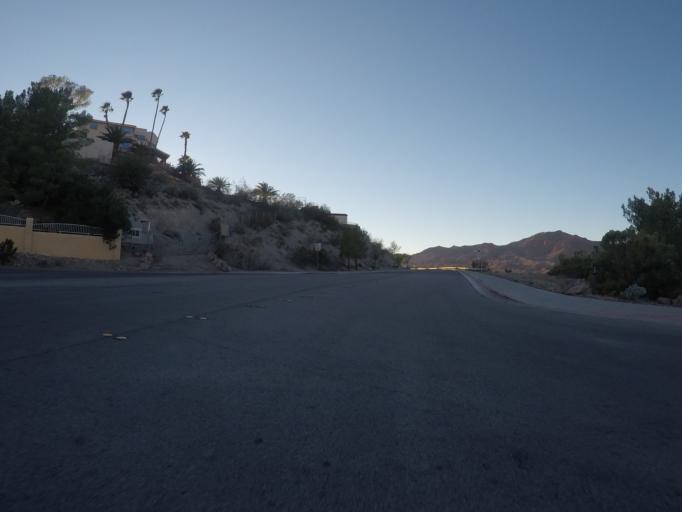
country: US
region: Nevada
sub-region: Clark County
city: Boulder City
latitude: 35.9814
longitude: -114.8324
